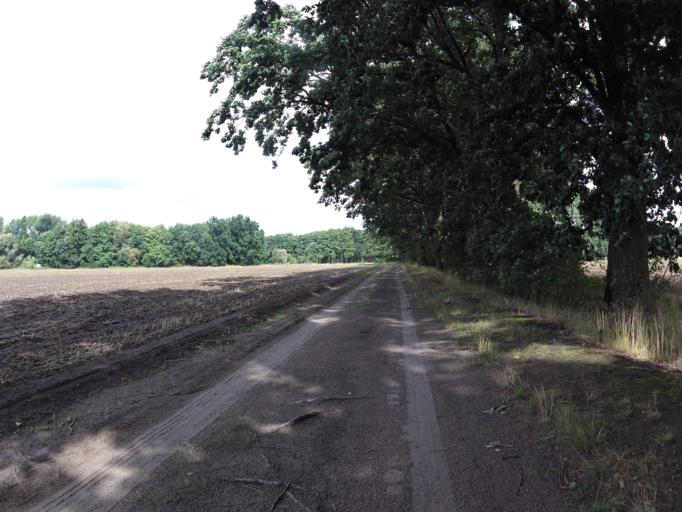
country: DE
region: Brandenburg
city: Storkow
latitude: 52.2746
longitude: 13.9339
